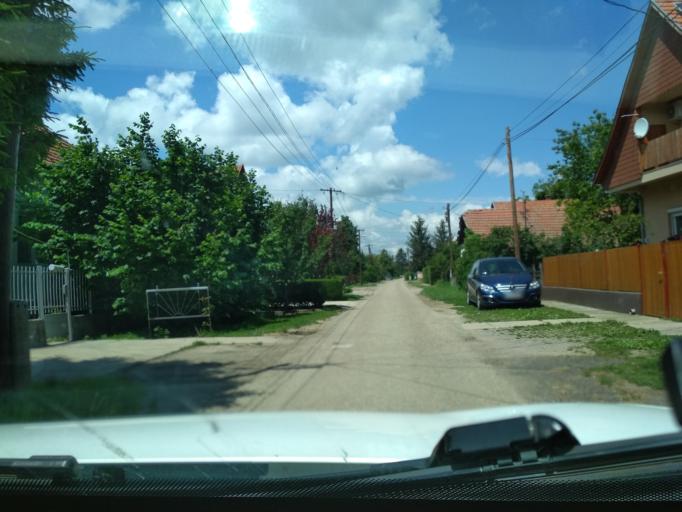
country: HU
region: Jasz-Nagykun-Szolnok
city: Tiszafured
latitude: 47.6015
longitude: 20.7567
